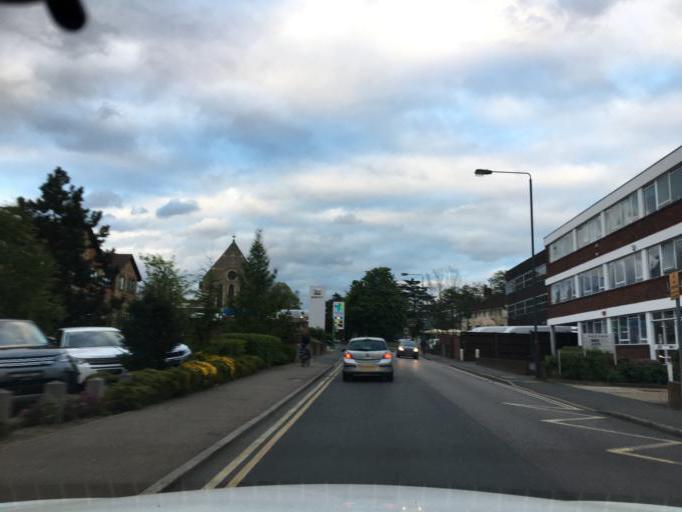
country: GB
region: England
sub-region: Greater London
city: Sidcup
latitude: 51.4272
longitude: 0.0948
